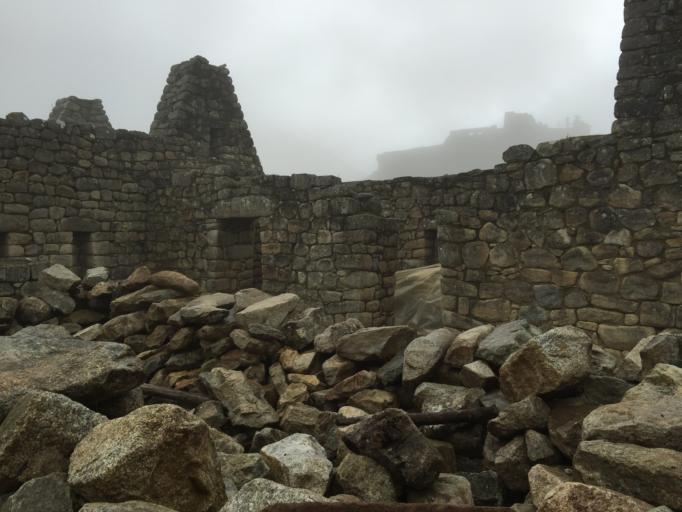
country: PE
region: Cusco
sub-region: Provincia de La Convencion
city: Santa Teresa
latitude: -13.1625
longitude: -72.5451
